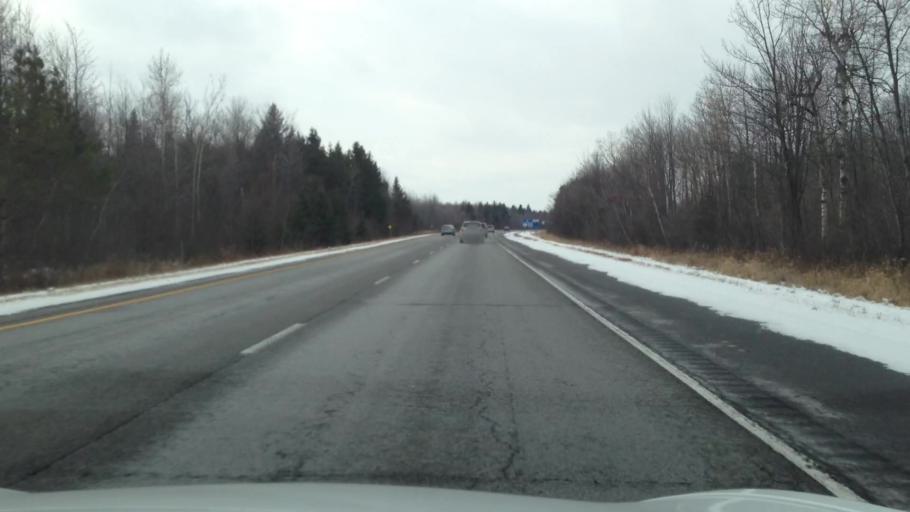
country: CA
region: Ontario
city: Casselman
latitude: 45.3134
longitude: -75.2080
